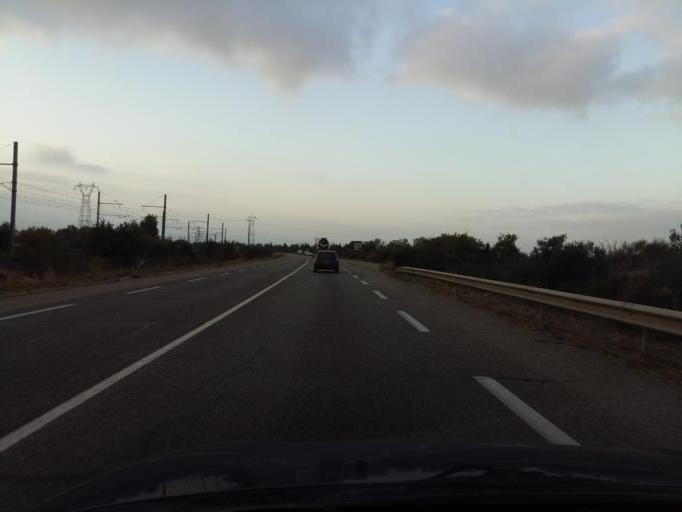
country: FR
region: Provence-Alpes-Cote d'Azur
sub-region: Departement des Bouches-du-Rhone
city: Istres
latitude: 43.5493
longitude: 4.9568
